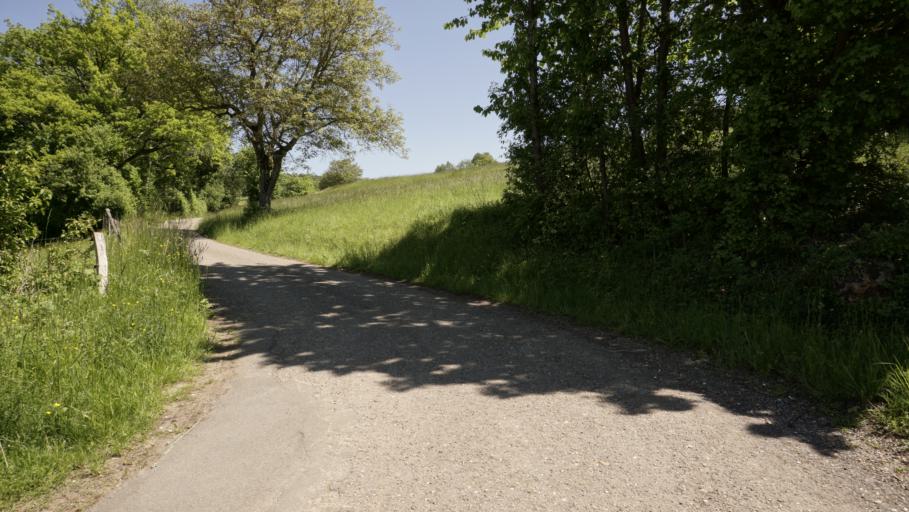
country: DE
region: Baden-Wuerttemberg
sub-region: Karlsruhe Region
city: Mosbach
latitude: 49.3695
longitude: 9.1750
